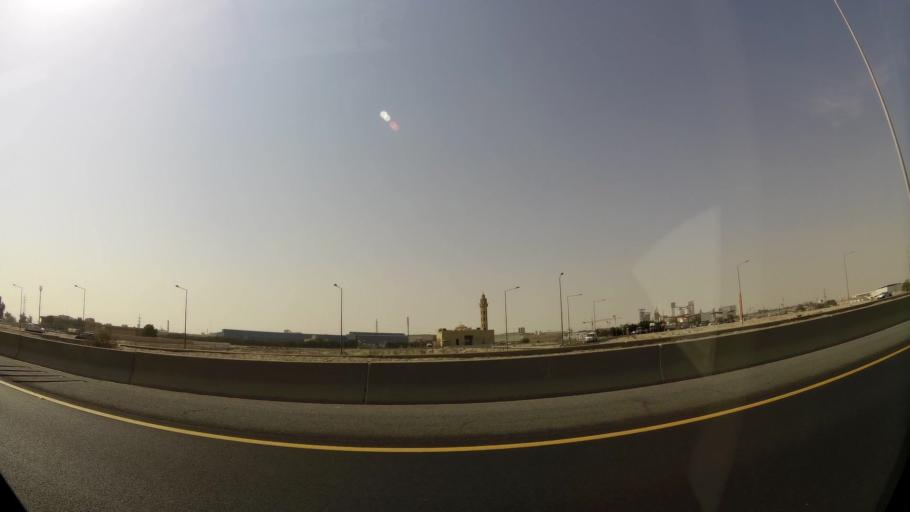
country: KW
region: Al Ahmadi
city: Al Fahahil
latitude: 29.0029
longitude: 48.1378
